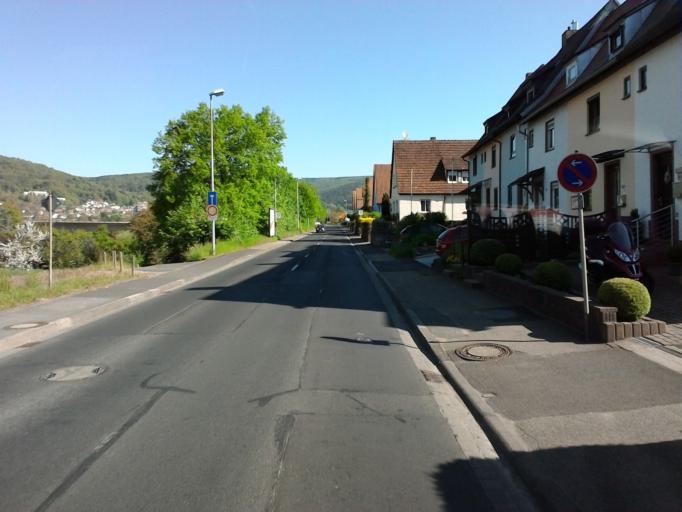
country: DE
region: Bavaria
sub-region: Regierungsbezirk Unterfranken
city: Lohr am Main
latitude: 49.9929
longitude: 9.5843
